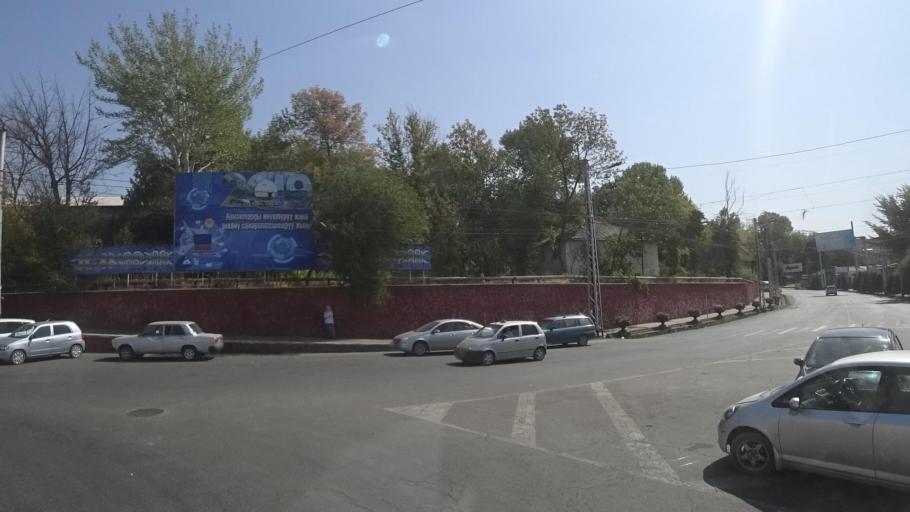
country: KG
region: Osh
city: Osh
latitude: 40.5142
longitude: 72.8138
